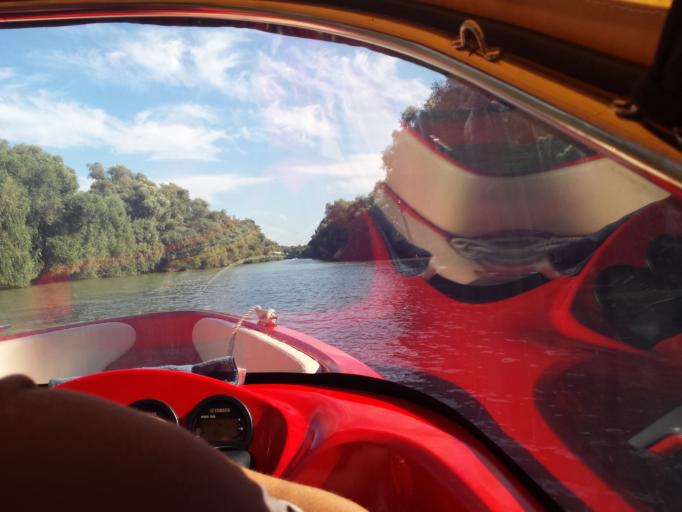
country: RO
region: Tulcea
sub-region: Comuna Pardina
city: Pardina
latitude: 45.2449
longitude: 28.9219
